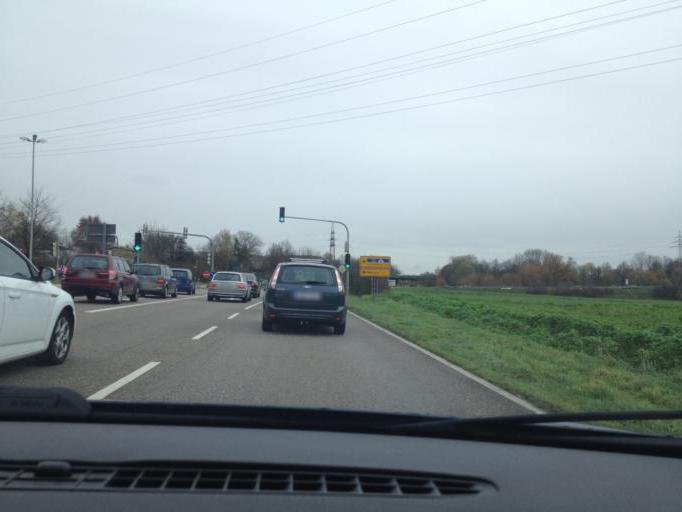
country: DE
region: Baden-Wuerttemberg
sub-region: Regierungsbezirk Stuttgart
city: Moglingen
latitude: 48.8863
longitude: 9.1409
